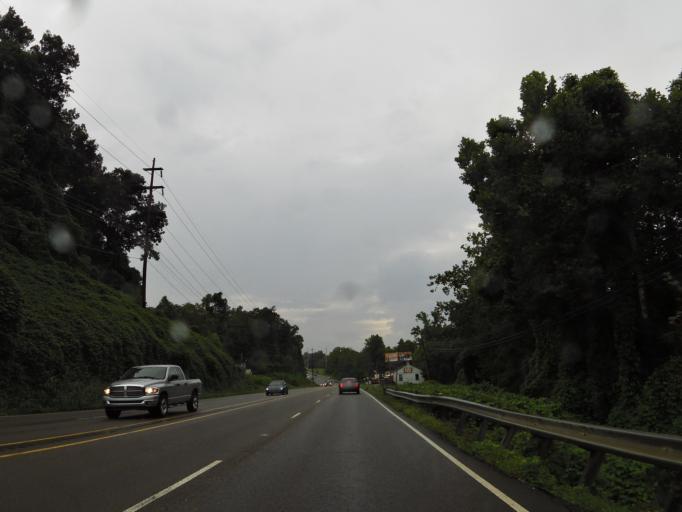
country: US
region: Tennessee
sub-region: Sevier County
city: Seymour
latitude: 35.9033
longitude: -83.8279
